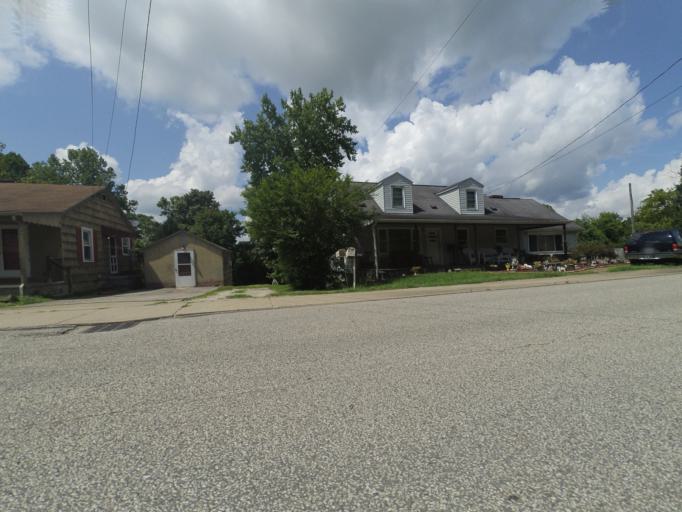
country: US
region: West Virginia
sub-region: Cabell County
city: Barboursville
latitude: 38.4098
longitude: -82.2846
